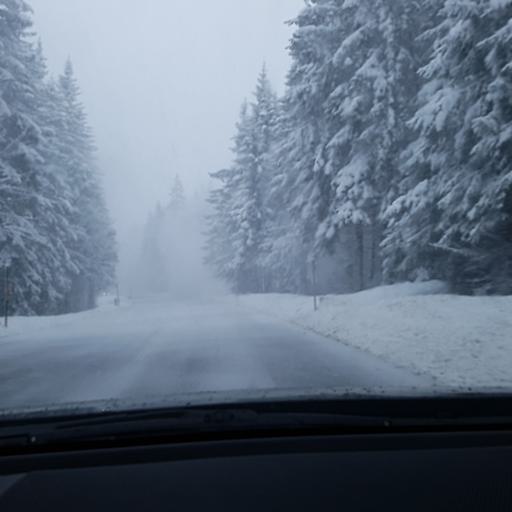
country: AT
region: Styria
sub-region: Politischer Bezirk Liezen
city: Altaussee
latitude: 47.6249
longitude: 13.6934
